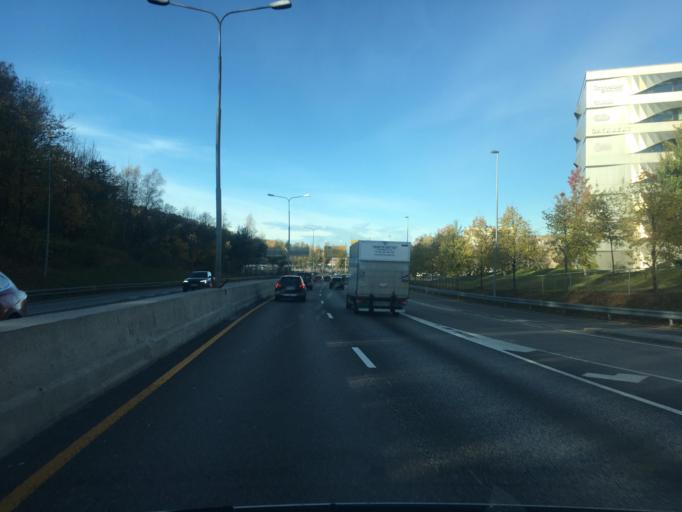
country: NO
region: Oslo
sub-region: Oslo
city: Oslo
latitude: 59.8887
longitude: 10.8060
